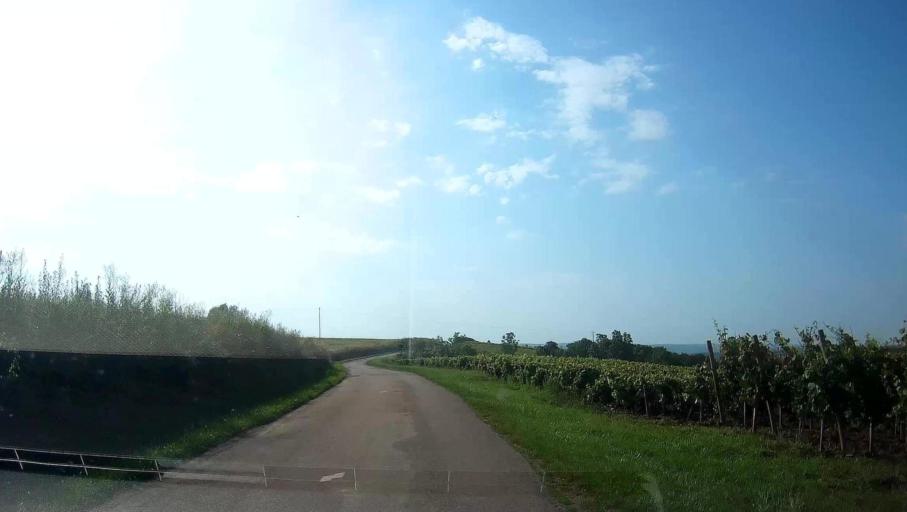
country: FR
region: Bourgogne
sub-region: Departement de Saone-et-Loire
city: Couches
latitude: 46.9031
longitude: 4.5980
